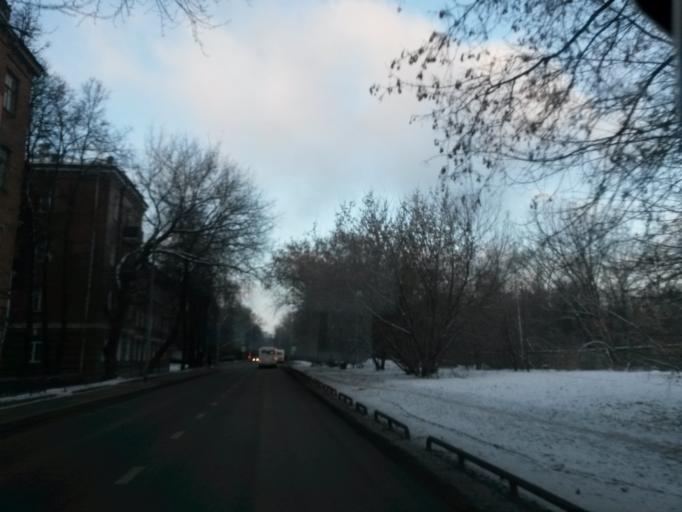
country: RU
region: Moskovskaya
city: Bol'shaya Setun'
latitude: 55.7116
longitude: 37.4423
